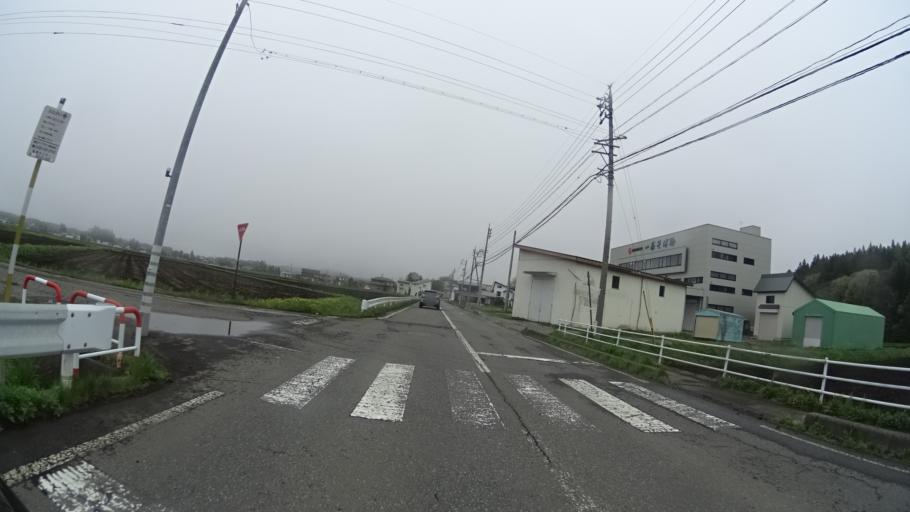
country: JP
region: Nagano
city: Nagano-shi
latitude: 36.7721
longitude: 138.2010
